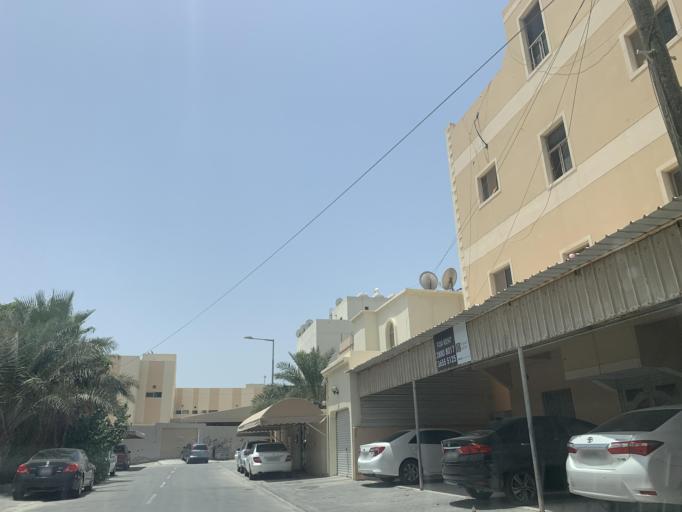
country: BH
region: Northern
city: Madinat `Isa
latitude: 26.1704
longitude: 50.5673
